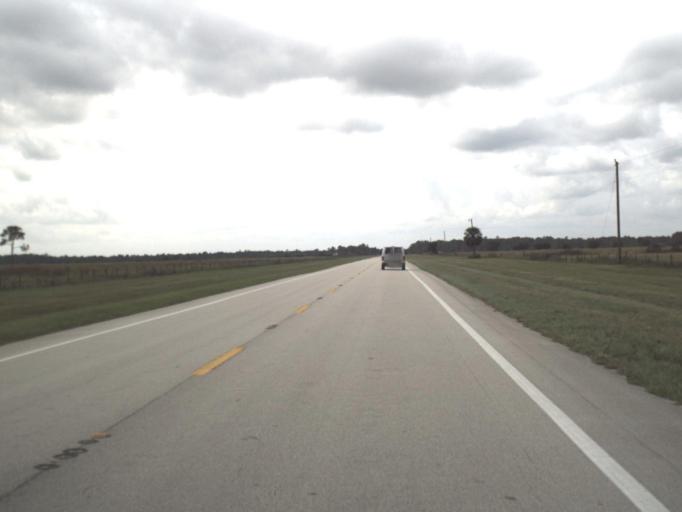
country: US
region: Florida
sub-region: Hendry County
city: Port LaBelle
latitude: 26.9052
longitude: -81.3328
